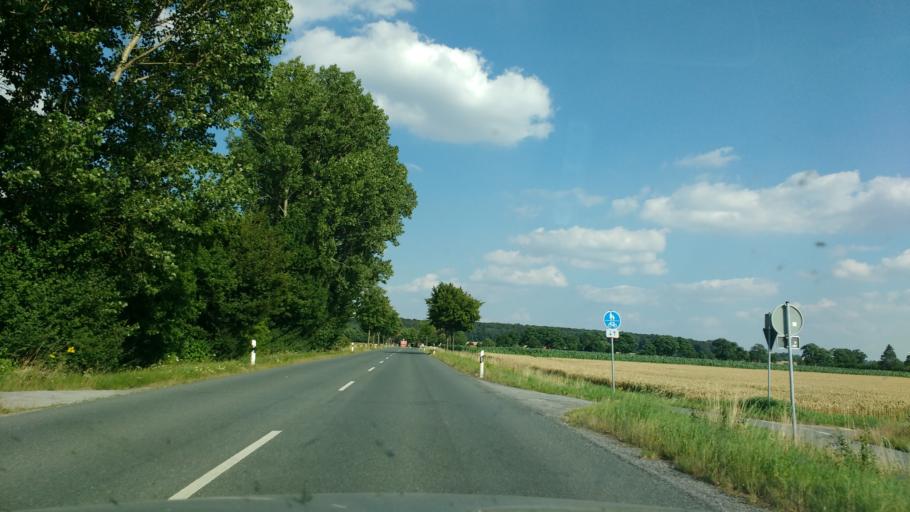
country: DE
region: North Rhine-Westphalia
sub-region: Regierungsbezirk Detmold
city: Salzkotten
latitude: 51.6663
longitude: 8.6353
